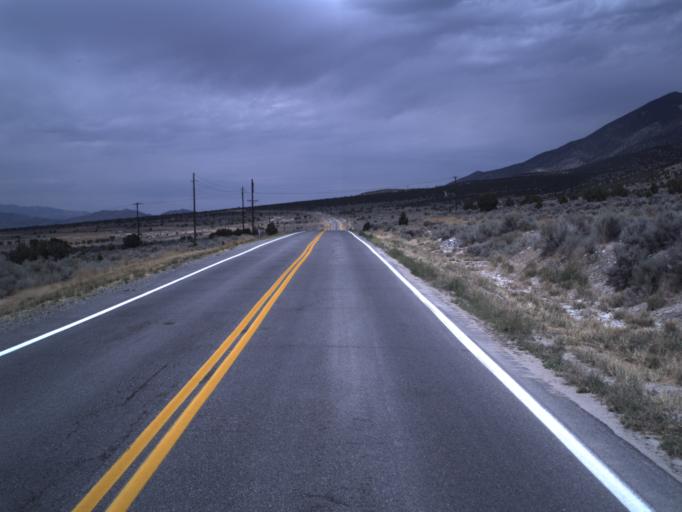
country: US
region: Utah
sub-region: Tooele County
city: Tooele
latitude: 40.3149
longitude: -112.2835
